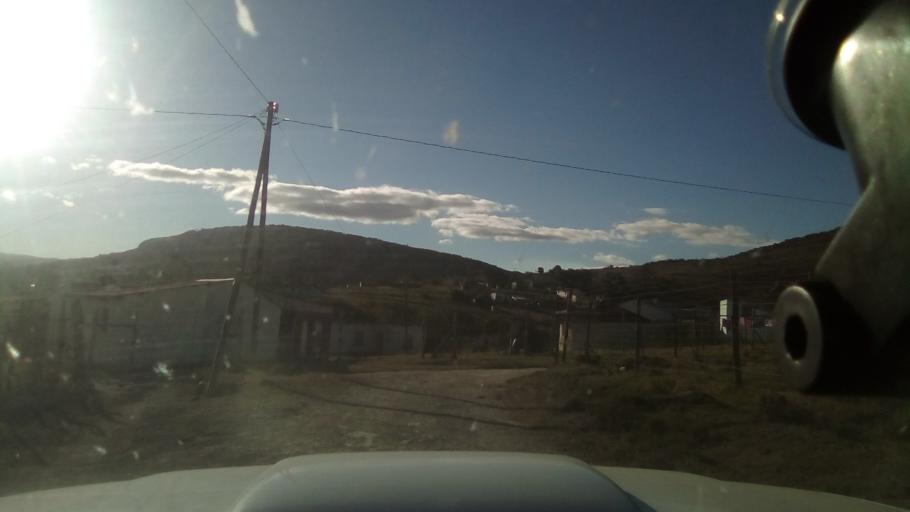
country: ZA
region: Eastern Cape
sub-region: Buffalo City Metropolitan Municipality
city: Bhisho
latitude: -32.7326
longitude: 27.3628
